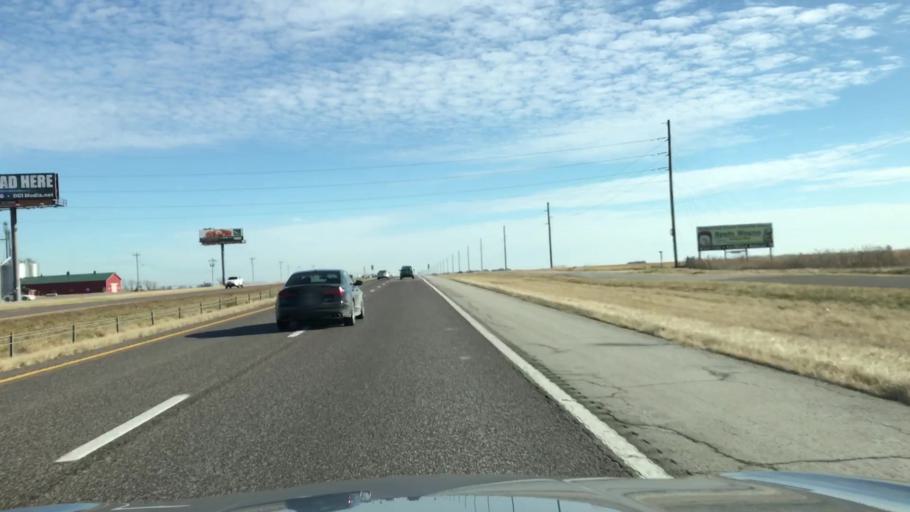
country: US
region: Missouri
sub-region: Callaway County
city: Fulton
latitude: 38.9528
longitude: -92.0803
